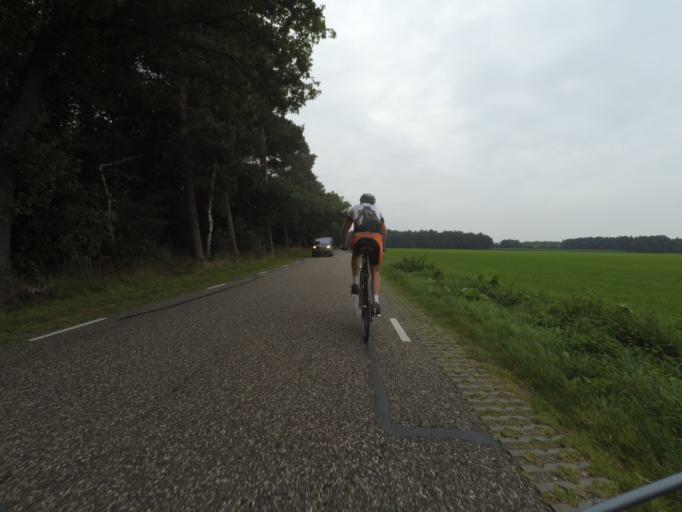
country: NL
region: Overijssel
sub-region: Gemeente Losser
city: Losser
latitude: 52.2935
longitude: 7.0197
